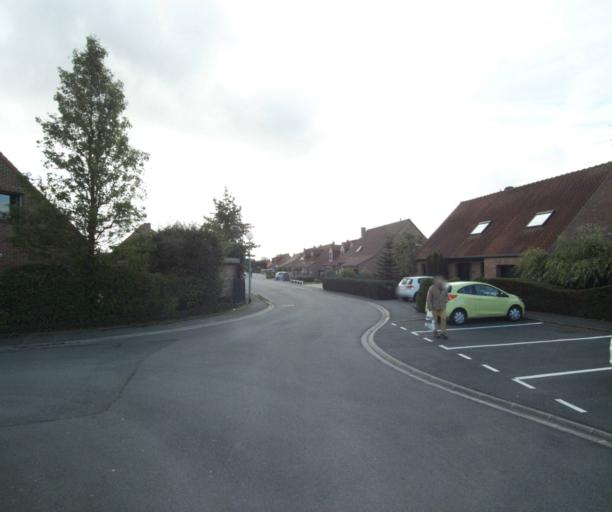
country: FR
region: Nord-Pas-de-Calais
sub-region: Departement du Nord
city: Houplines
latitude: 50.6926
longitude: 2.9202
